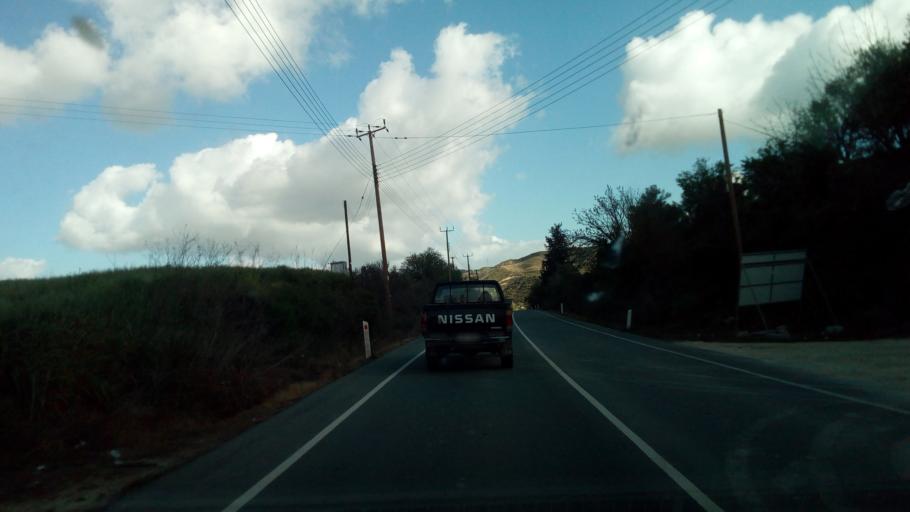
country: CY
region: Pafos
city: Polis
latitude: 34.9478
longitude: 32.4679
